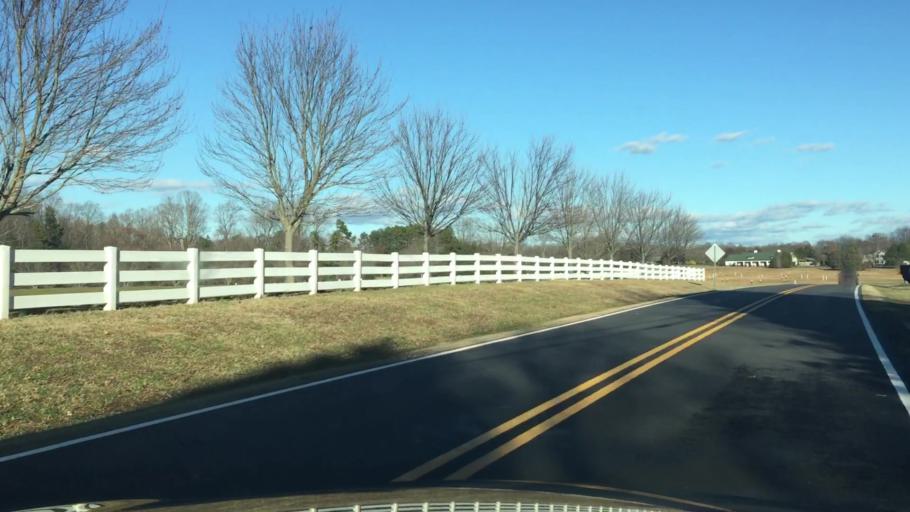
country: US
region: North Carolina
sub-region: Mecklenburg County
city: Cornelius
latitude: 35.5240
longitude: -80.8820
